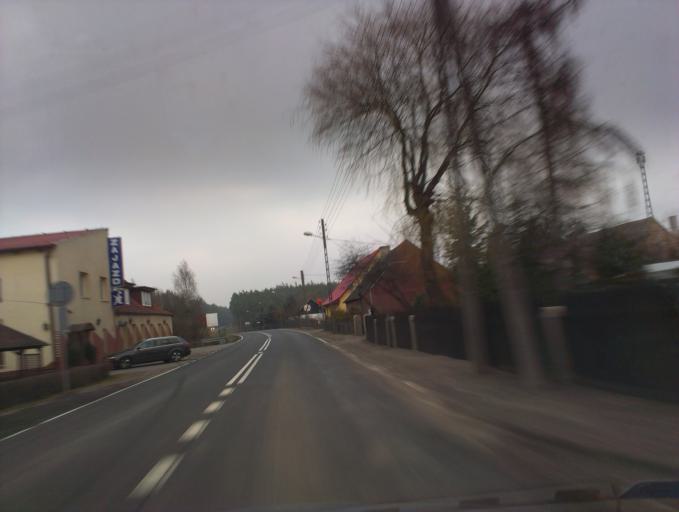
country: PL
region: Greater Poland Voivodeship
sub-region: Powiat zlotowski
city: Tarnowka
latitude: 53.3088
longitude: 16.7935
